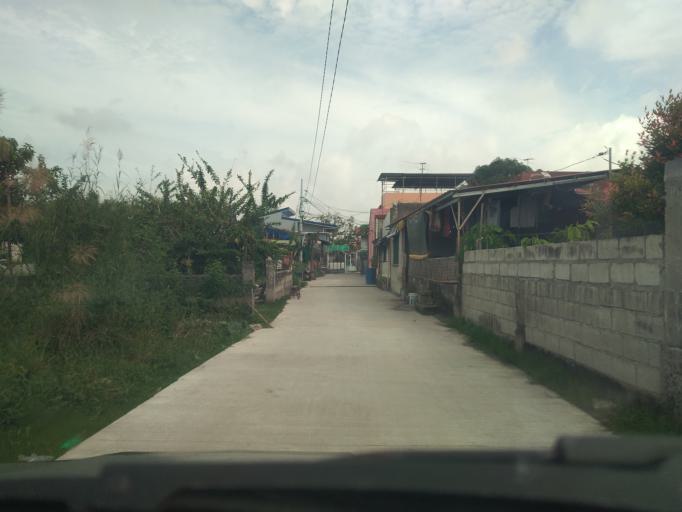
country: PH
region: Central Luzon
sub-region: Province of Pampanga
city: Pau
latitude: 15.0036
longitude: 120.7135
